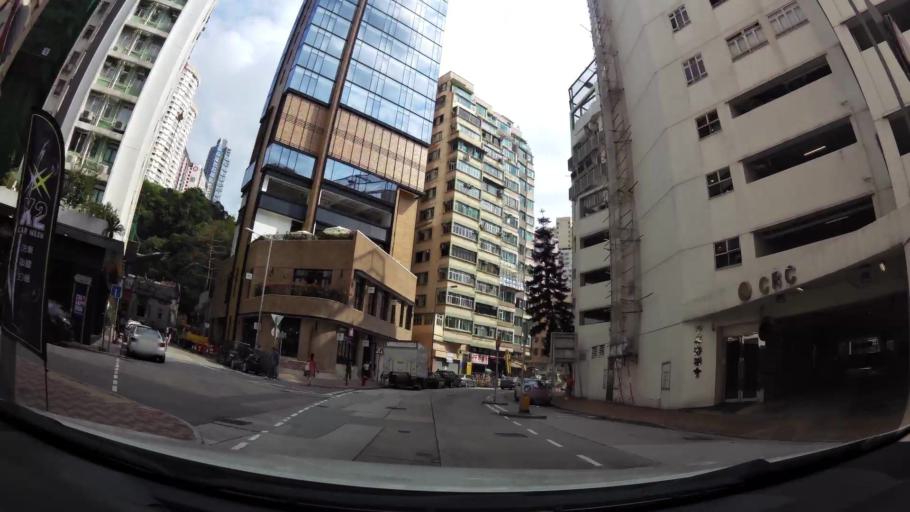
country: HK
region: Wanchai
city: Wan Chai
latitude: 22.2803
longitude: 114.1922
